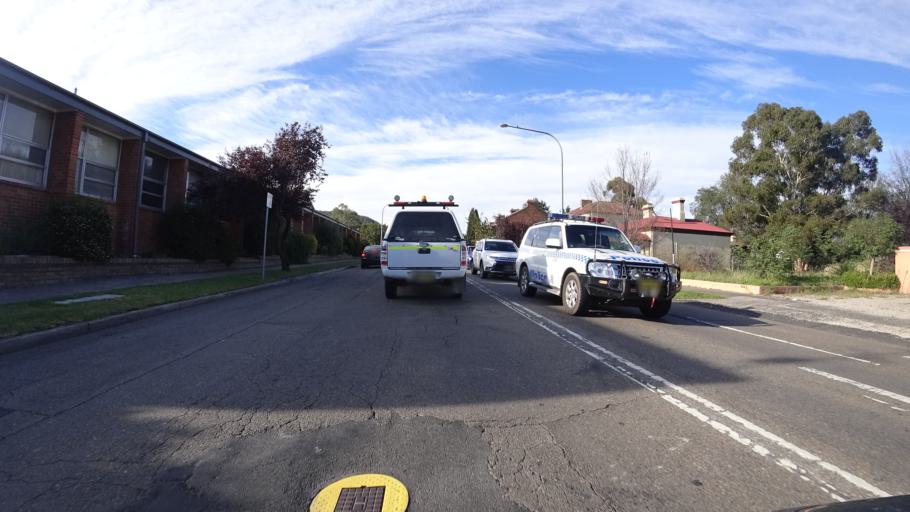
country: AU
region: New South Wales
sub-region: Lithgow
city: Lithgow
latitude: -33.4839
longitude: 150.1530
